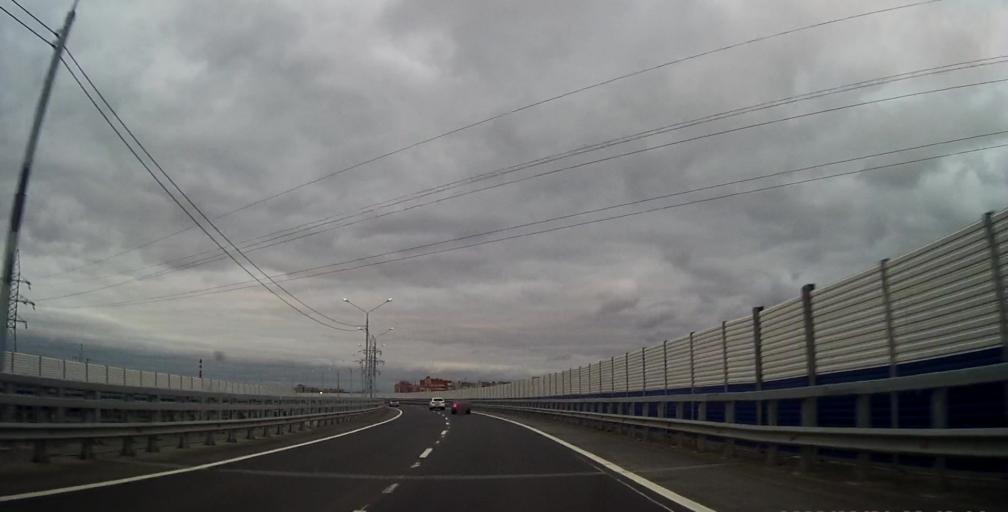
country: RU
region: Moskovskaya
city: Klimovsk
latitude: 55.3814
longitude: 37.5267
